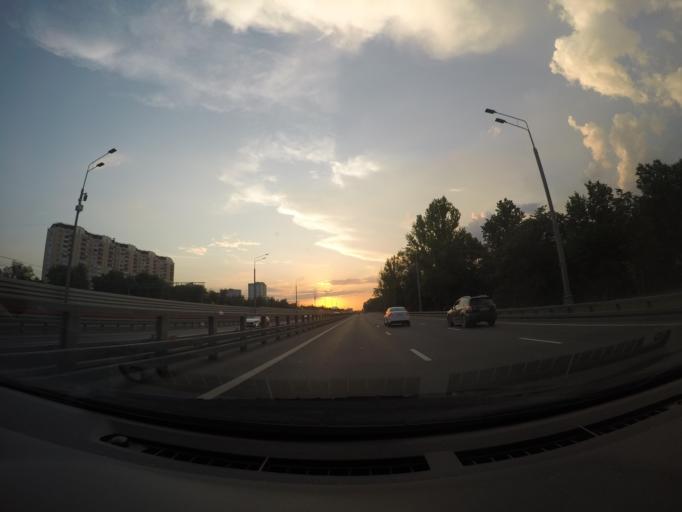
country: RU
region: Moscow
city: Veshnyaki
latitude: 55.7191
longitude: 37.8100
